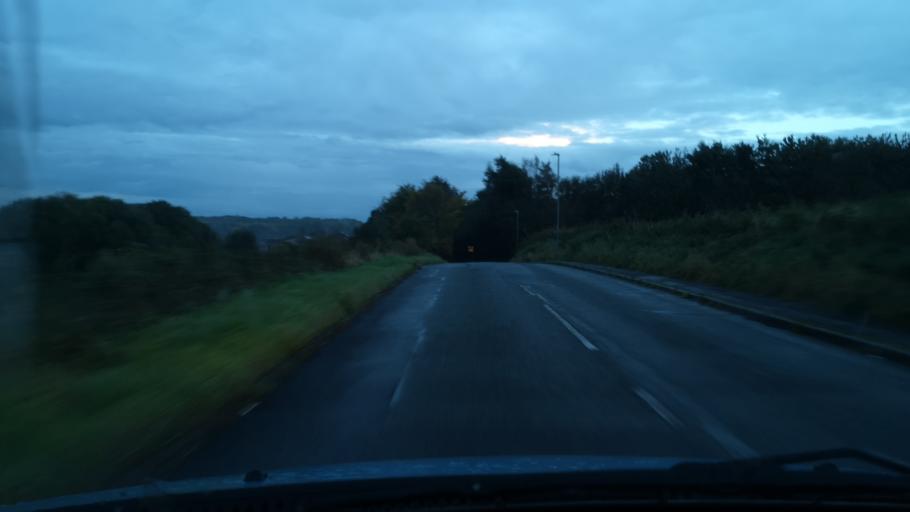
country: GB
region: England
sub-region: Kirklees
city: Batley
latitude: 53.7290
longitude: -1.6380
